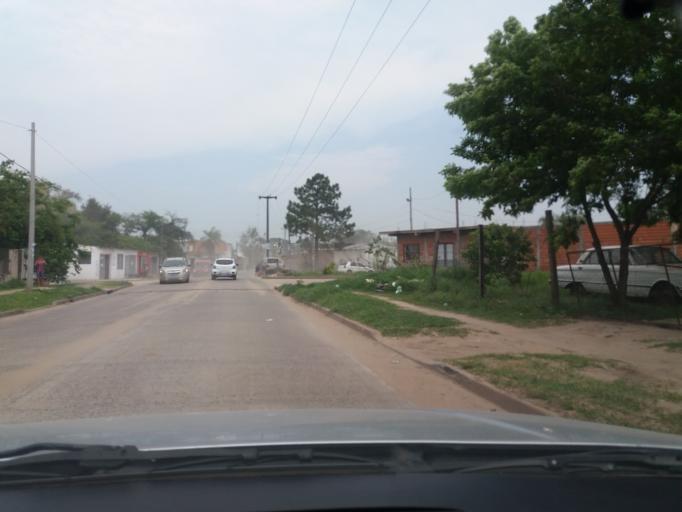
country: AR
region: Corrientes
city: Corrientes
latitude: -27.5120
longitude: -58.8020
